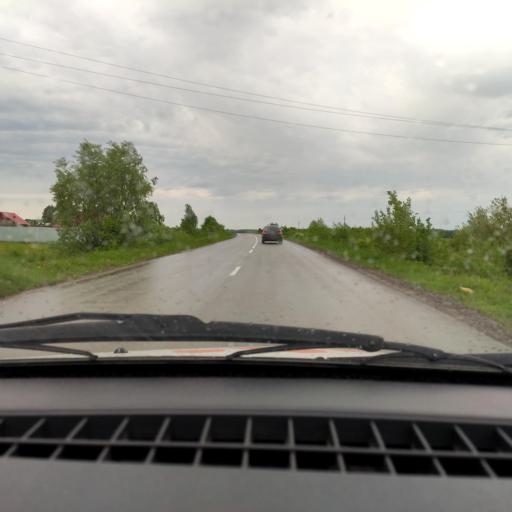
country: RU
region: Bashkortostan
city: Kudeyevskiy
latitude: 54.8433
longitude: 56.7958
